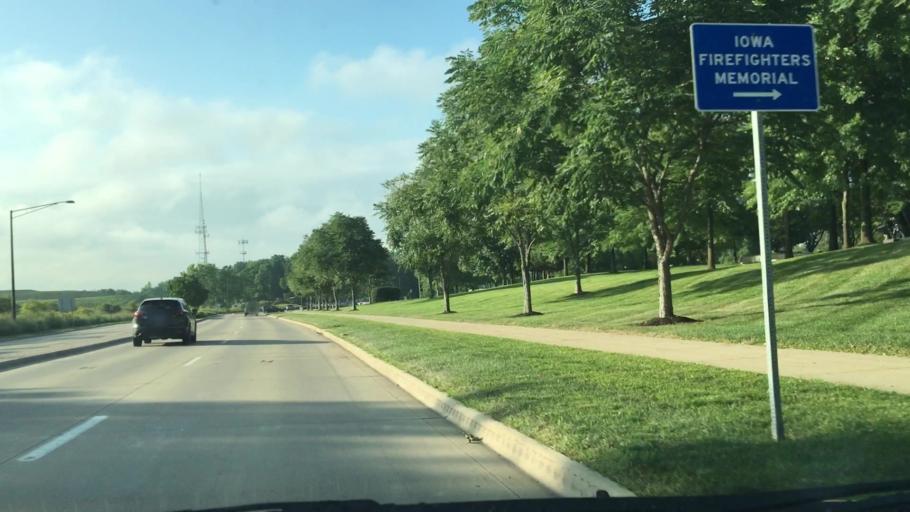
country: US
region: Iowa
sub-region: Johnson County
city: Coralville
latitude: 41.6915
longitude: -91.5660
